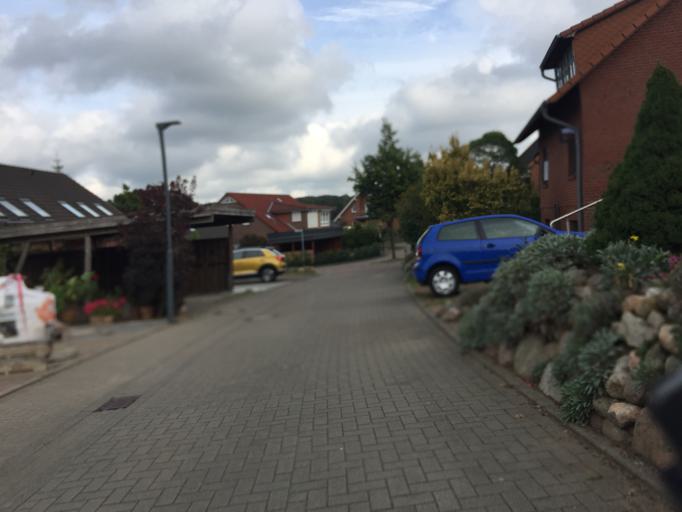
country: DE
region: Schleswig-Holstein
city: Itzehoe
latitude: 53.9324
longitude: 9.5324
